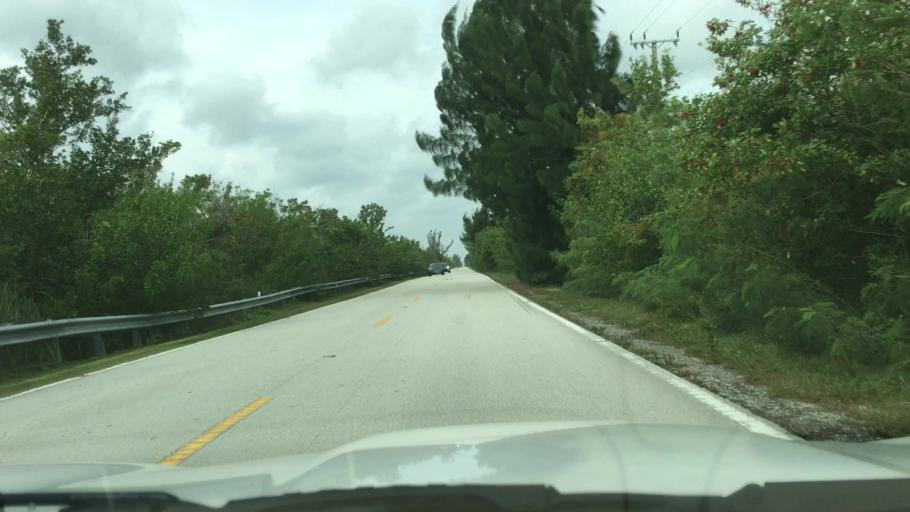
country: US
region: Florida
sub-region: Monroe County
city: North Key Largo
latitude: 25.3376
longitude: -80.4107
